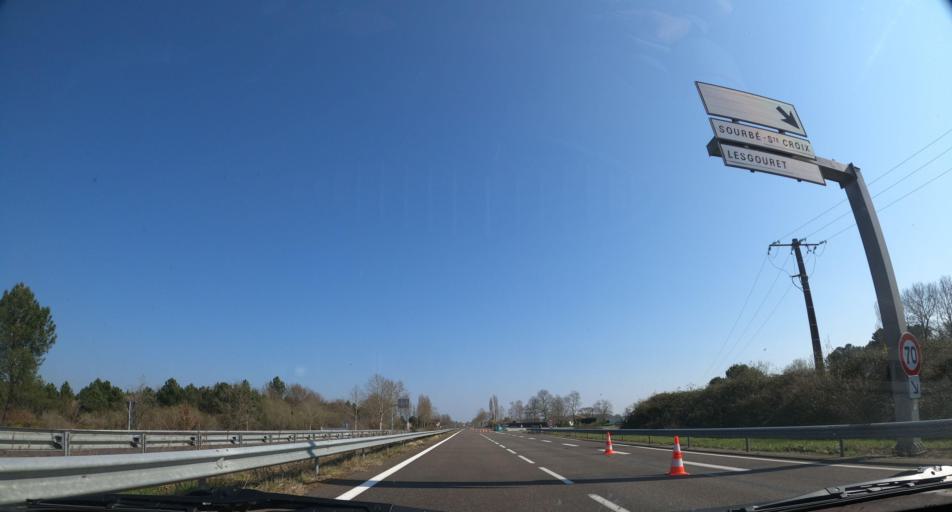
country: FR
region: Aquitaine
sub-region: Departement des Landes
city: Meilhan
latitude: 43.8567
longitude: -0.7248
